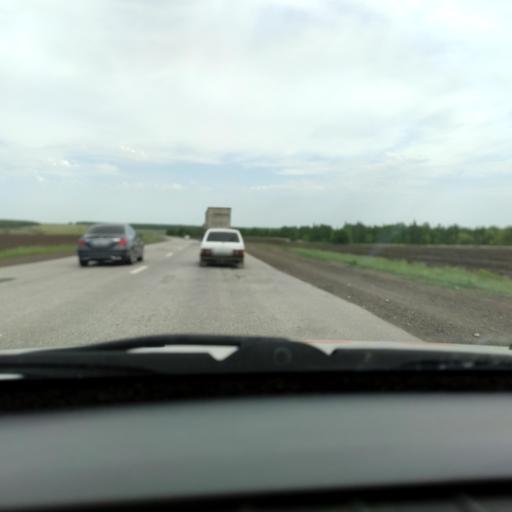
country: RU
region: Samara
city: Yelkhovka
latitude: 53.7236
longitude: 50.2331
